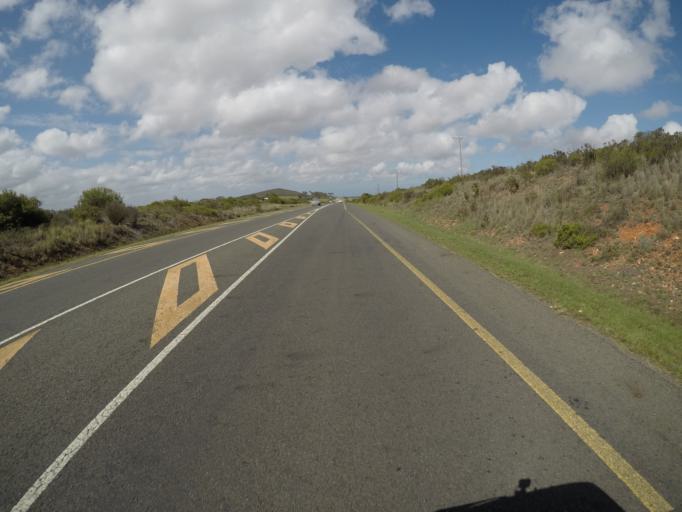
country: ZA
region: Western Cape
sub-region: Eden District Municipality
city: Mossel Bay
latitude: -34.1955
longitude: 21.7986
